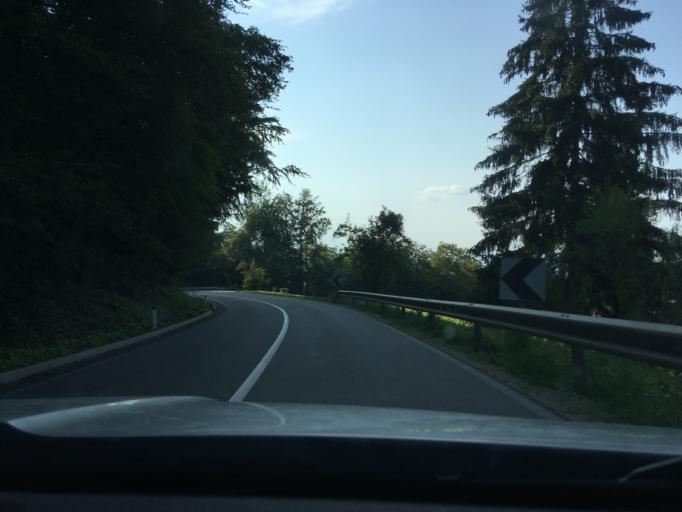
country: SI
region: Novo Mesto
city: Novo Mesto
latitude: 45.7313
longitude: 15.2290
